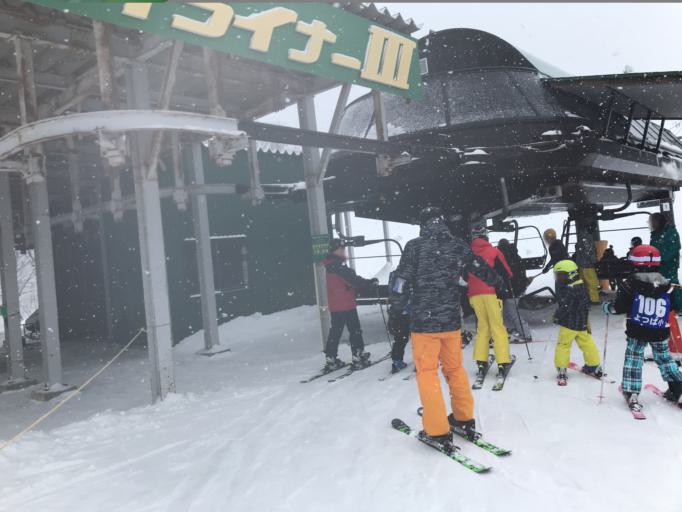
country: JP
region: Nagano
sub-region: Kitaazumi Gun
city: Hakuba
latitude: 36.7458
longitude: 137.8694
